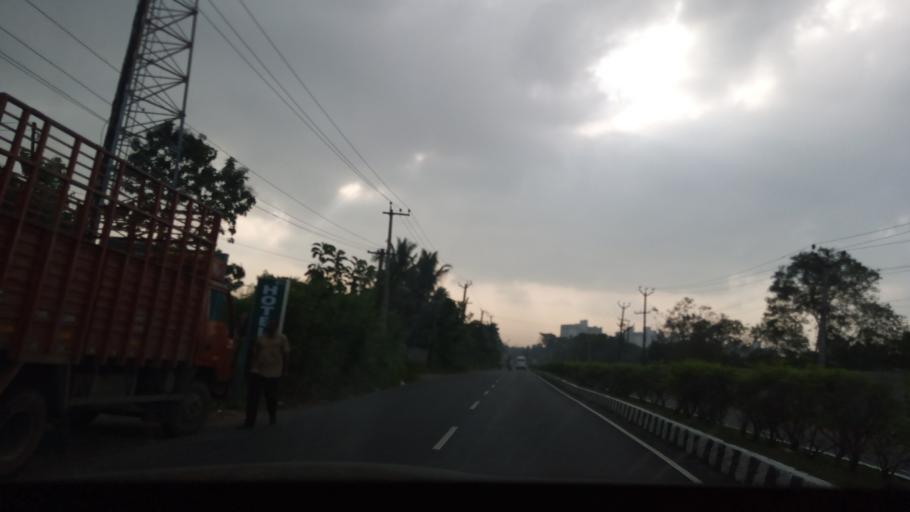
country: IN
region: Tamil Nadu
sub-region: Kancheepuram
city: Vengavasal
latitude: 12.8014
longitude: 80.1954
